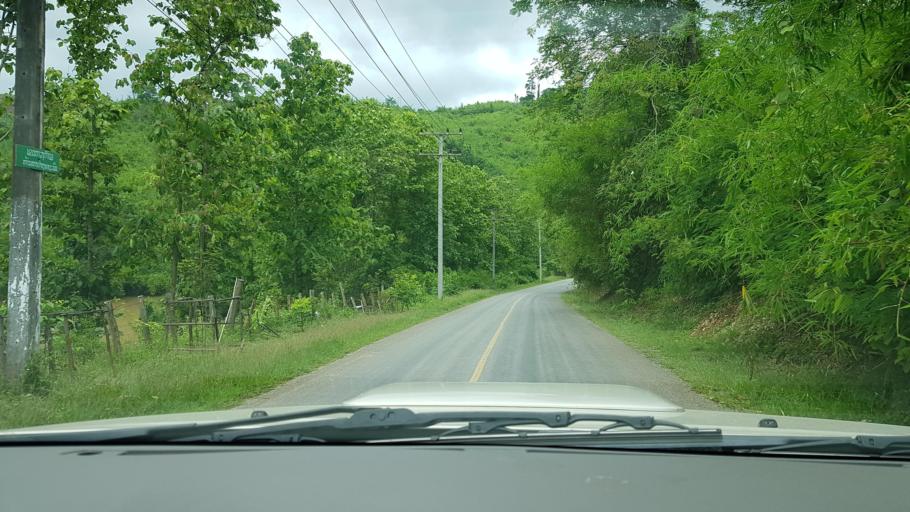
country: TH
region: Nan
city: Chaloem Phra Kiat
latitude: 19.9497
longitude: 101.2515
